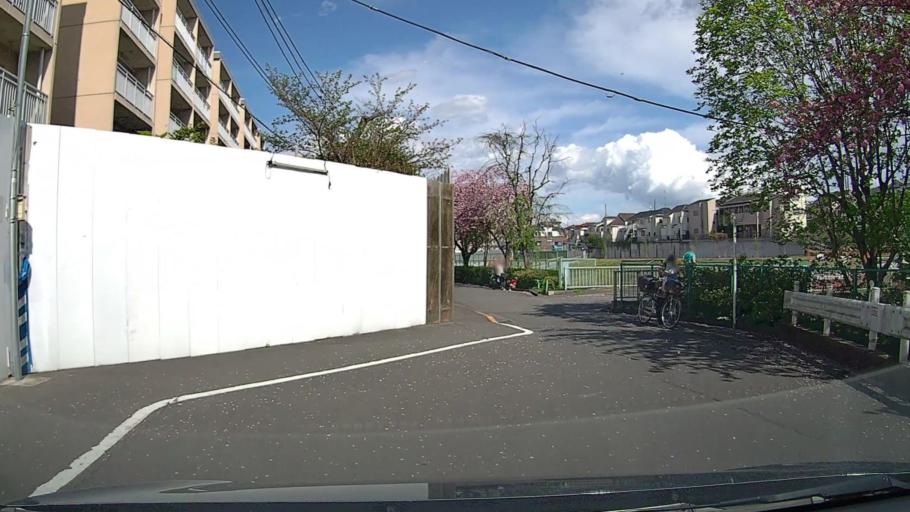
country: JP
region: Tokyo
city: Musashino
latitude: 35.7307
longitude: 139.5836
